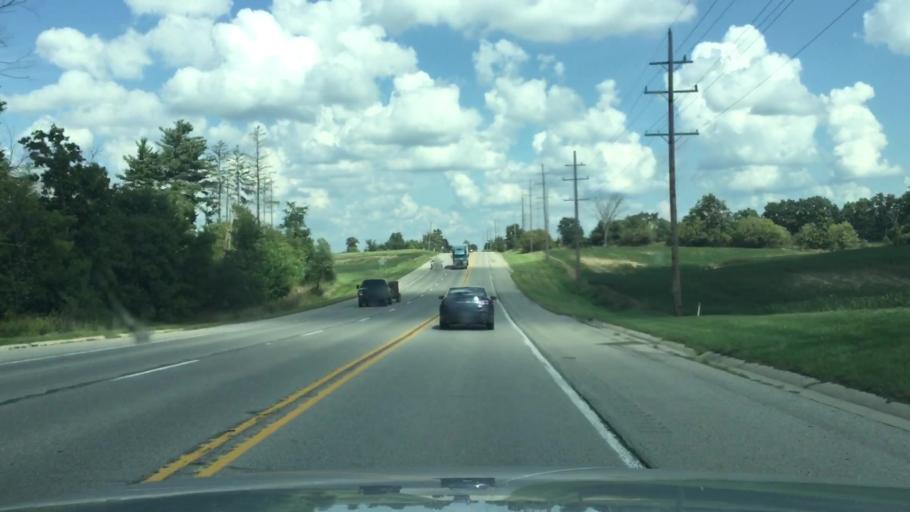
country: US
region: Michigan
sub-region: Washtenaw County
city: Saline
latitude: 42.1389
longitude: -83.8477
